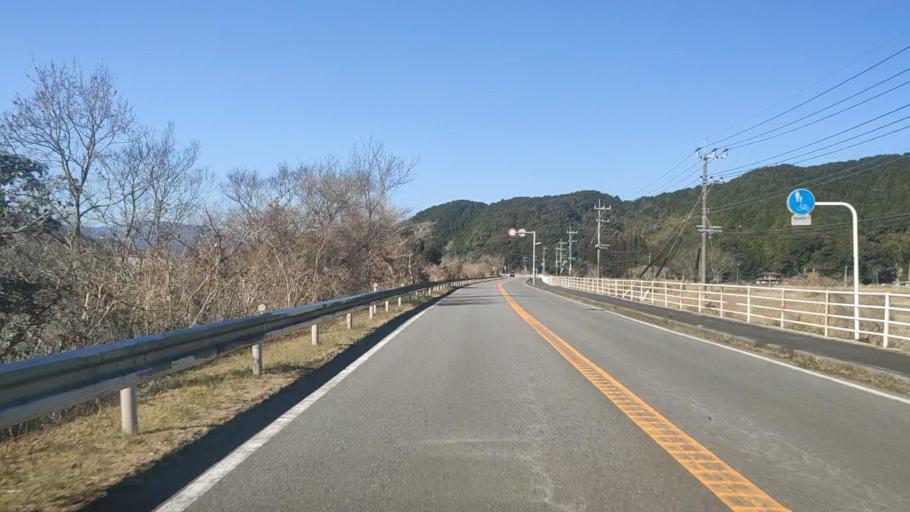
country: JP
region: Oita
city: Saiki
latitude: 32.9374
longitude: 131.9164
